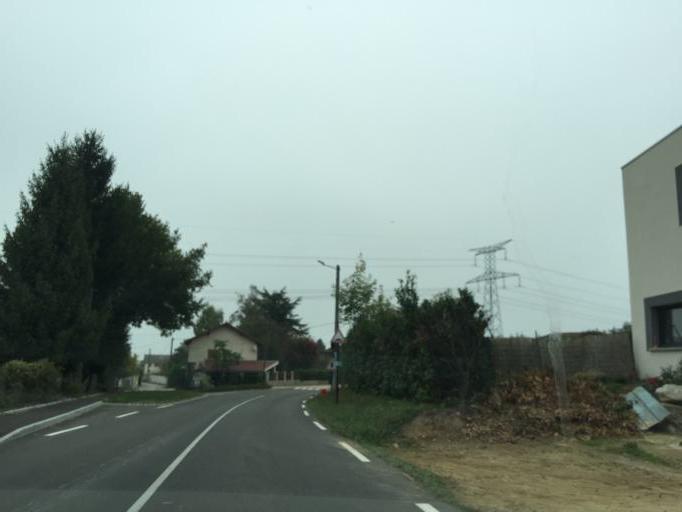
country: FR
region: Rhone-Alpes
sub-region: Departement de l'Isere
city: Faverges-de-la-Tour
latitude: 45.5889
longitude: 5.5134
